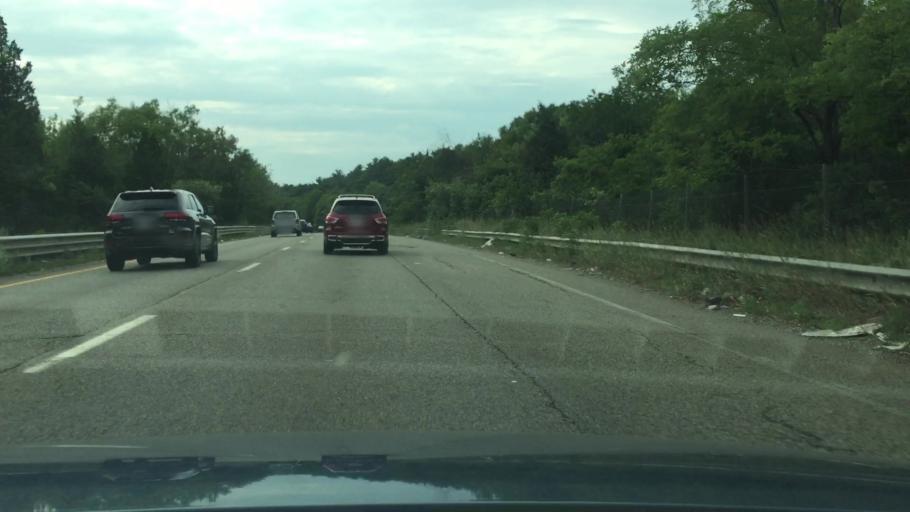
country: US
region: Massachusetts
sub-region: Plymouth County
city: North Pembroke
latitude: 42.1167
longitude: -70.7787
